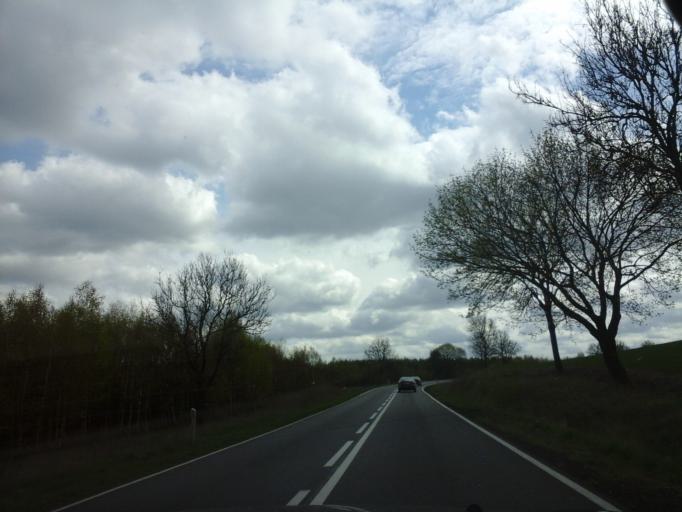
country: PL
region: West Pomeranian Voivodeship
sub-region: Powiat choszczenski
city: Pelczyce
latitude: 53.0639
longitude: 15.3008
